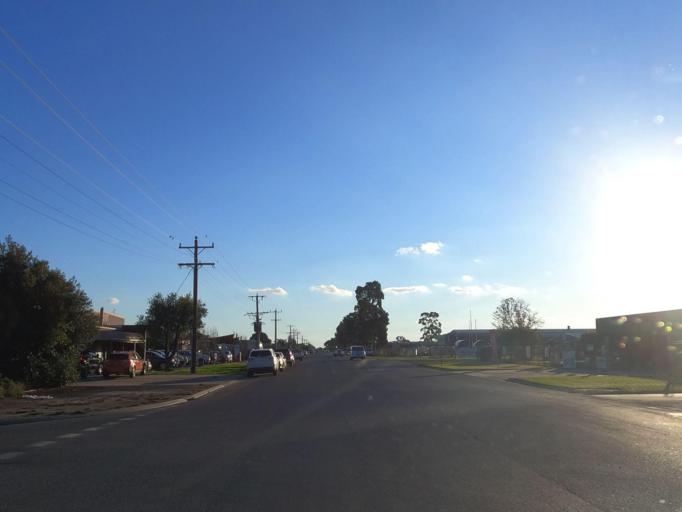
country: AU
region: Victoria
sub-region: Swan Hill
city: Swan Hill
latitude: -35.3265
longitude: 143.5463
